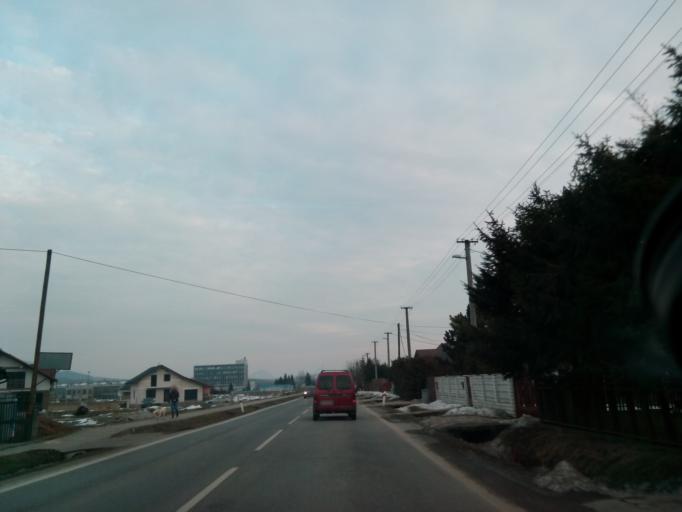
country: SK
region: Presovsky
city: Sabinov
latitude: 49.1207
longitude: 21.0530
